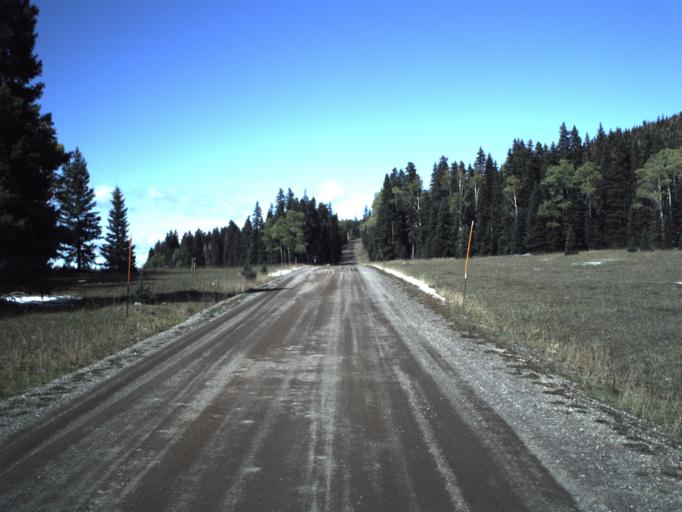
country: US
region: Utah
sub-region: Piute County
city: Junction
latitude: 38.2500
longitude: -112.3745
